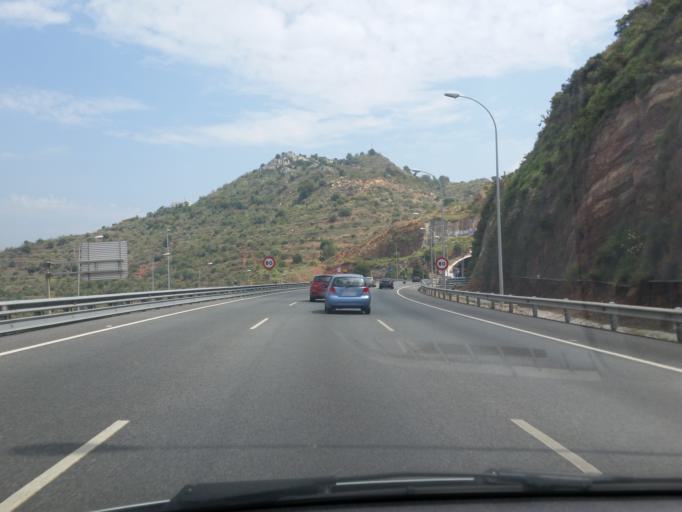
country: ES
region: Andalusia
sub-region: Provincia de Malaga
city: Malaga
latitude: 36.7397
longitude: -4.3878
